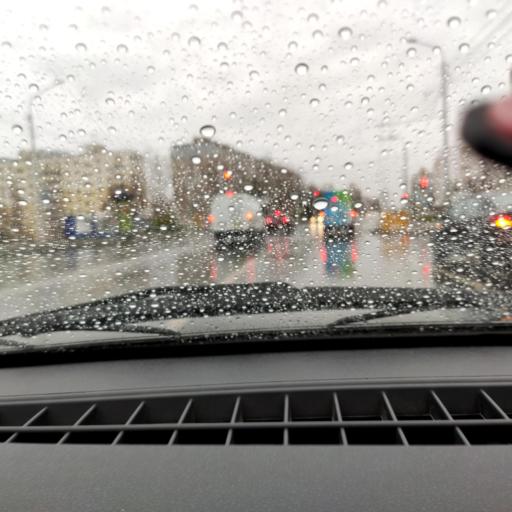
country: RU
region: Bashkortostan
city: Ufa
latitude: 54.7703
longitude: 56.0327
